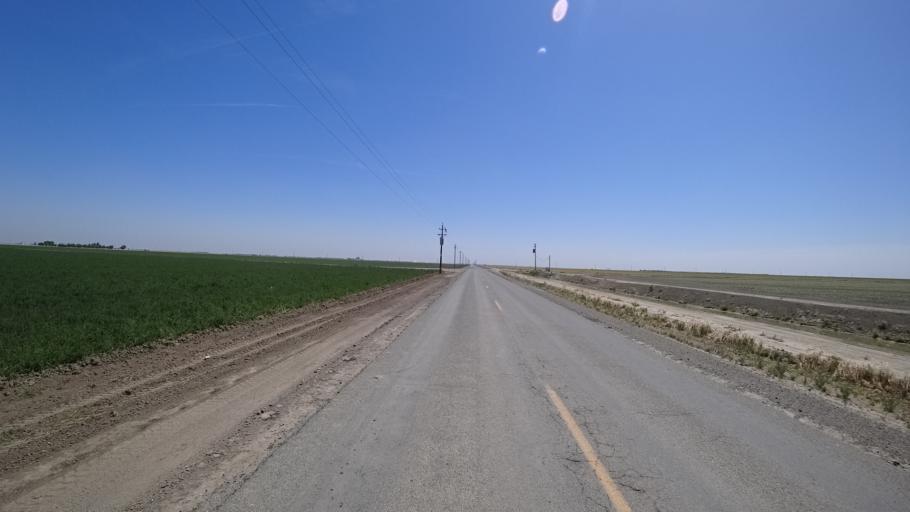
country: US
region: California
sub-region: Kings County
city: Corcoran
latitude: 36.0215
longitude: -119.5826
